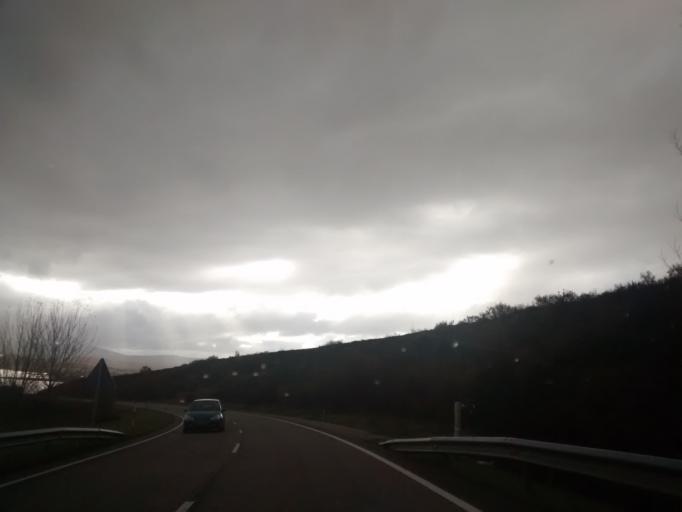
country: ES
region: Castille and Leon
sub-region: Provincia de Burgos
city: Arija
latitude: 43.0259
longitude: -3.9762
